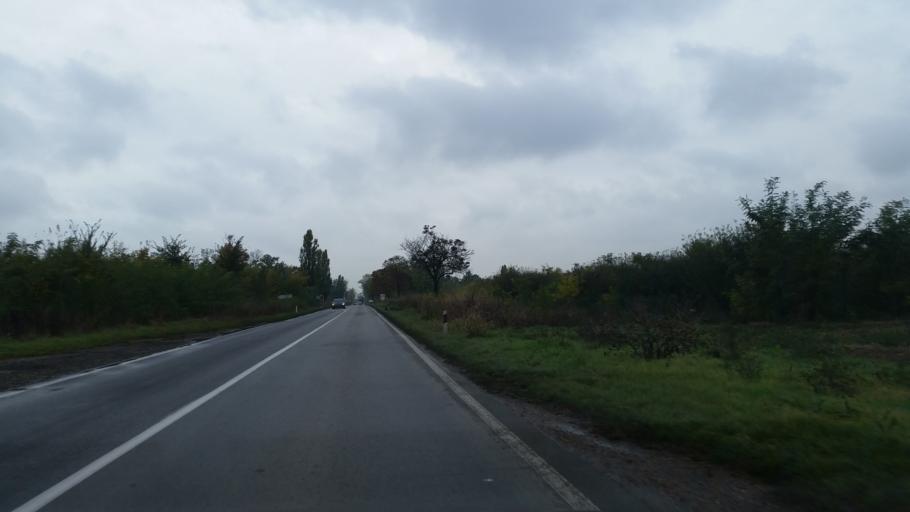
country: RS
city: Ecka
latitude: 45.3328
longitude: 20.4371
